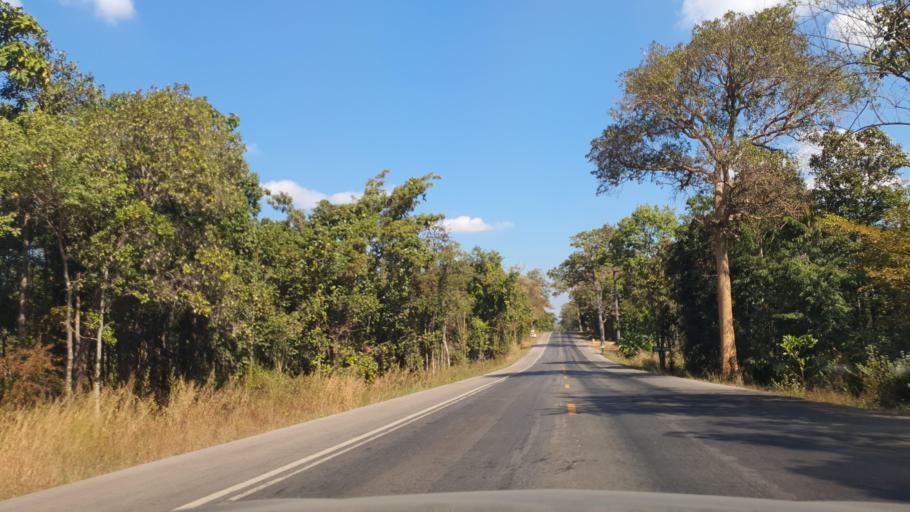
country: TH
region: Sakon Nakhon
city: Phu Phan
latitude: 16.9706
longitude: 103.9430
